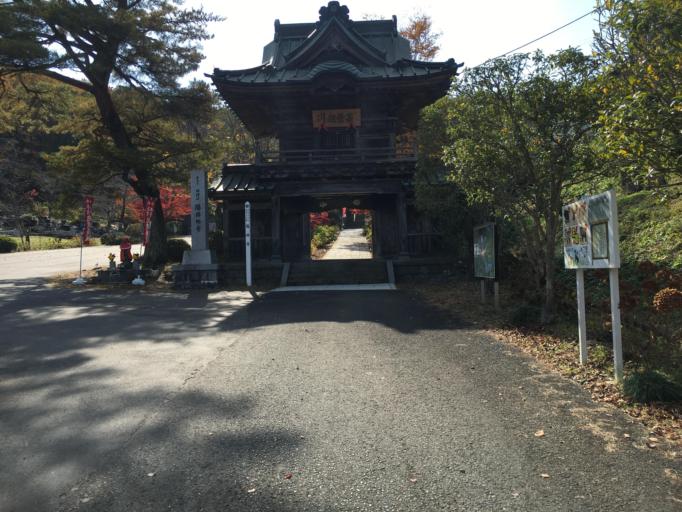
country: JP
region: Fukushima
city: Fukushima-shi
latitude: 37.7004
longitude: 140.4330
